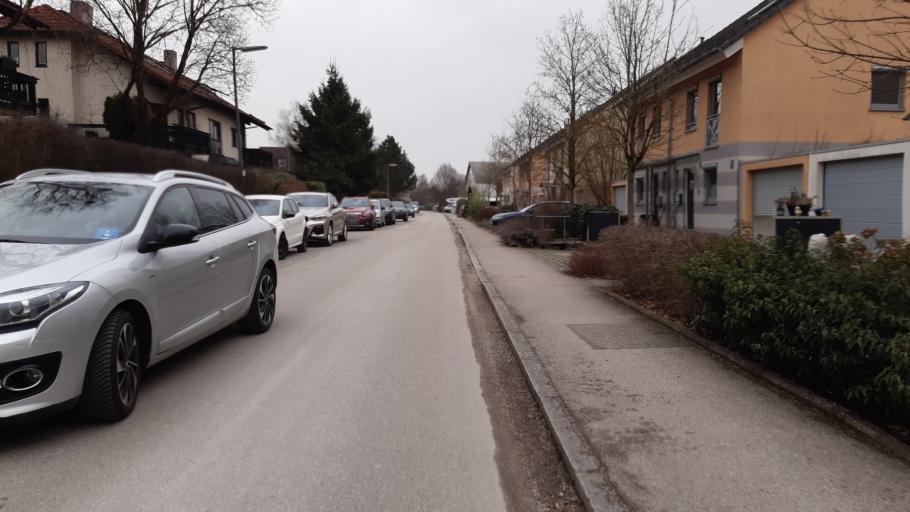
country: DE
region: Bavaria
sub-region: Upper Bavaria
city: Karlsfeld
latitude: 48.1966
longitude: 11.5134
